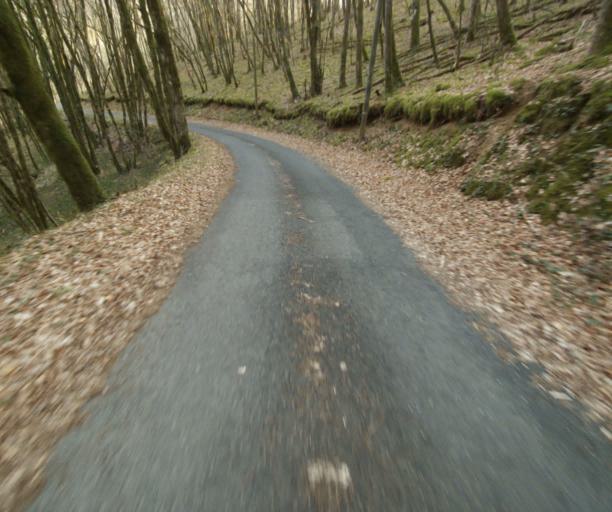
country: FR
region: Limousin
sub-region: Departement de la Correze
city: Correze
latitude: 45.3590
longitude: 1.8311
